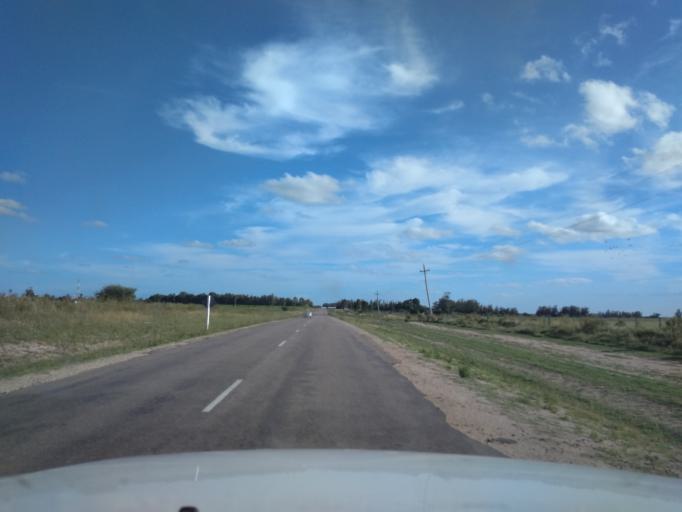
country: UY
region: Canelones
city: San Ramon
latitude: -34.2336
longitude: -55.9278
